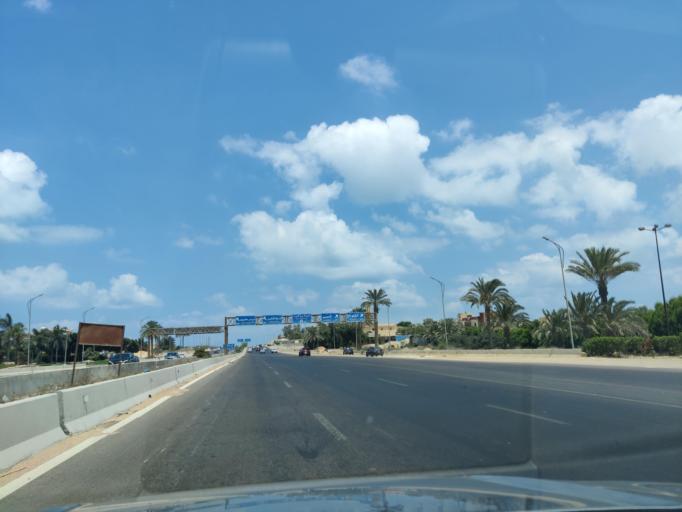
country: EG
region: Alexandria
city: Alexandria
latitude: 31.0076
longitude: 29.6385
